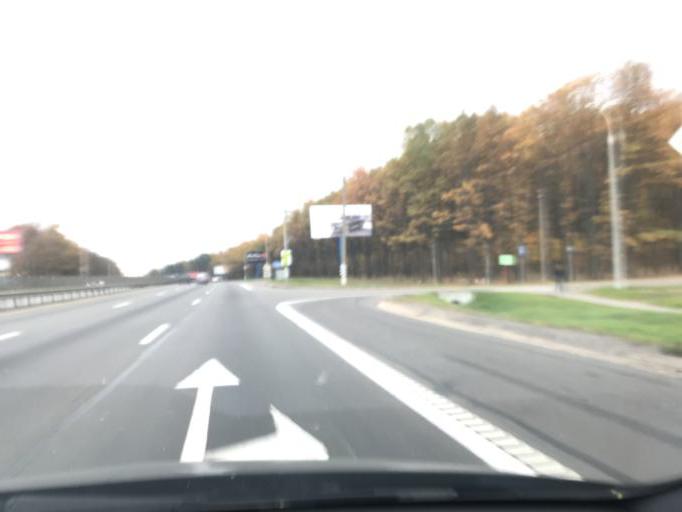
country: BY
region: Minsk
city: Hatava
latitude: 53.8335
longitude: 27.6378
